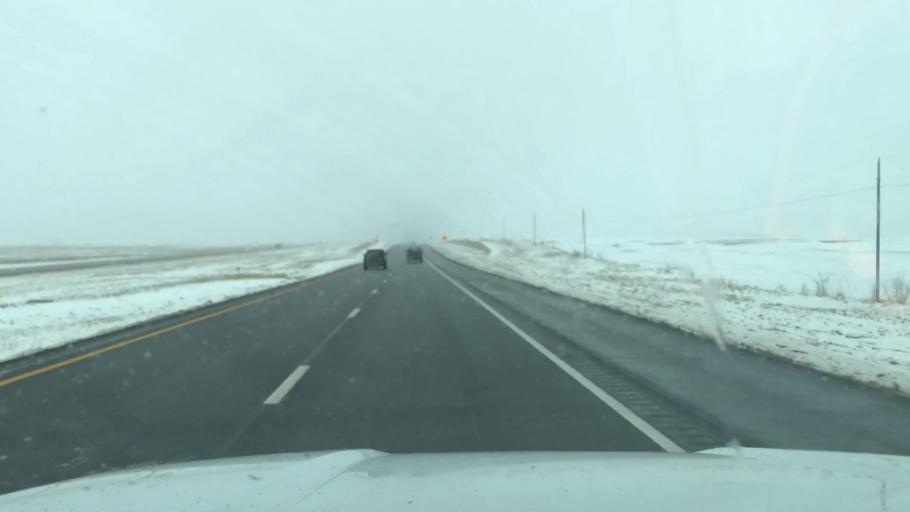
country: US
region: Missouri
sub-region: DeKalb County
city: Maysville
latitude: 39.7615
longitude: -94.3714
